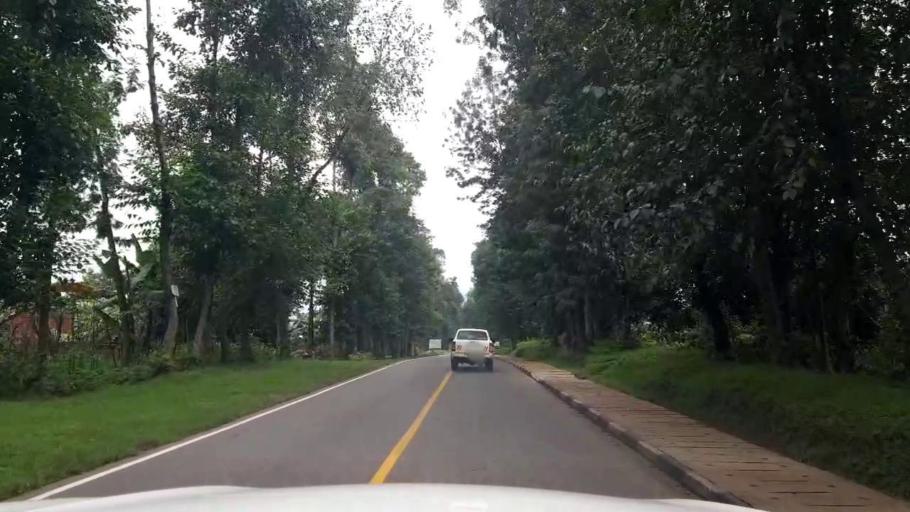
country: RW
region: Northern Province
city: Musanze
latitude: -1.4647
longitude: 29.6150
